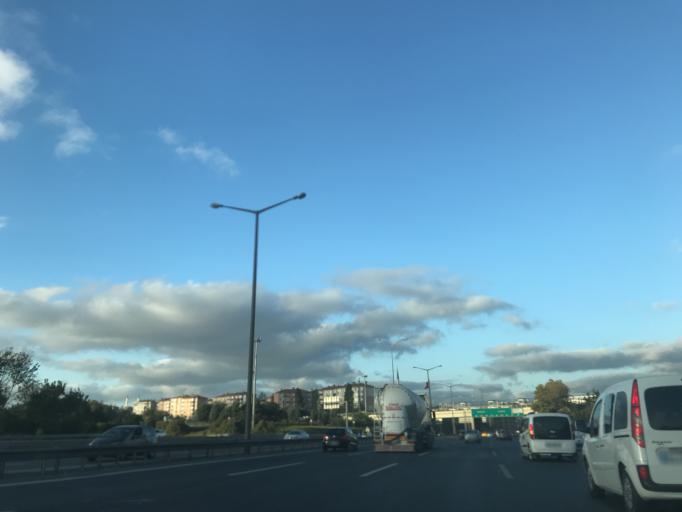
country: TR
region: Istanbul
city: Sultangazi
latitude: 41.0792
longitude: 28.8729
